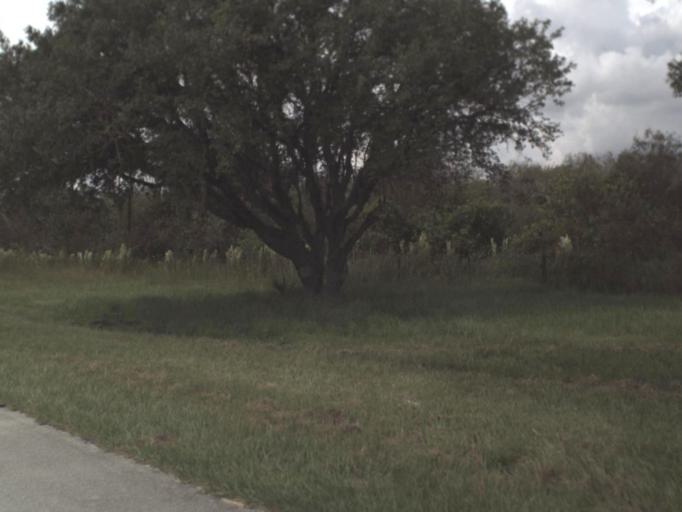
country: US
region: Florida
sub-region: Hendry County
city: Port LaBelle
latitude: 26.8155
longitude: -81.4102
